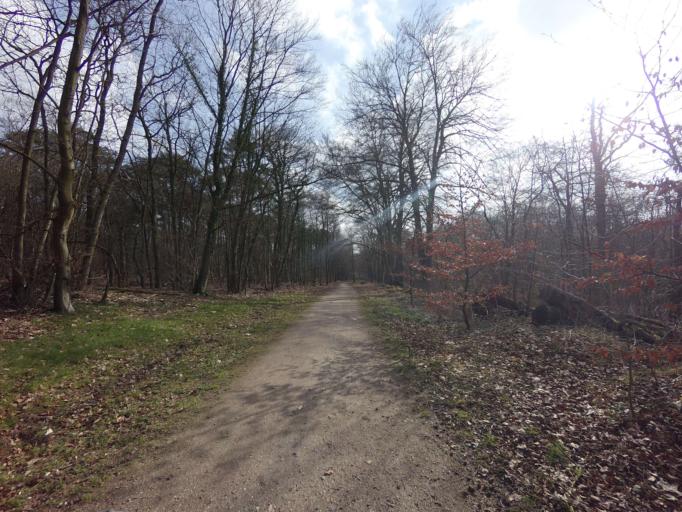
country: NL
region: North Holland
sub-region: Gemeente Bussum
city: Bussum
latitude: 52.2435
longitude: 5.1513
